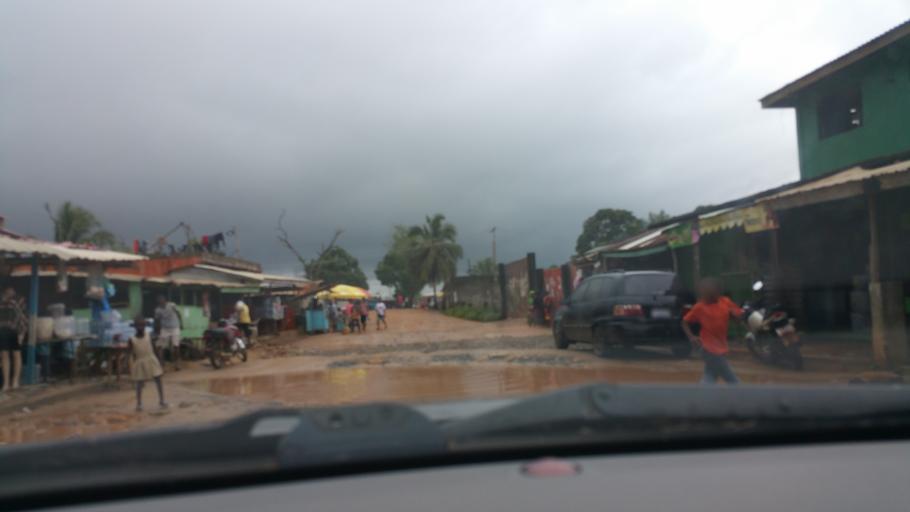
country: LR
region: Montserrado
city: Monrovia
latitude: 6.2332
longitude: -10.6693
